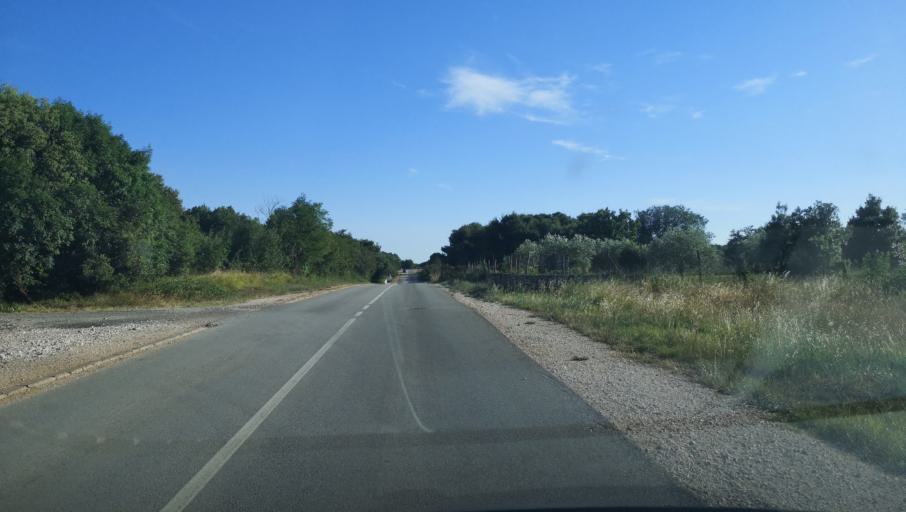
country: HR
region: Istarska
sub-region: Grad Rovinj
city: Rovinj
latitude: 45.0595
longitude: 13.6889
